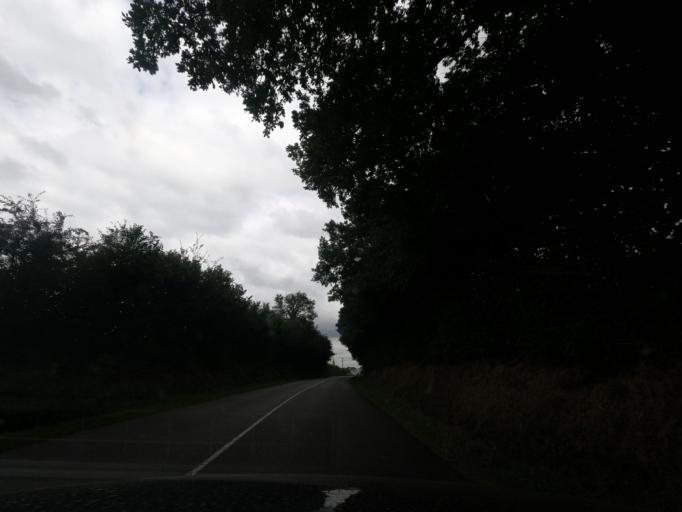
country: FR
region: Lower Normandy
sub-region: Departement de l'Orne
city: Briouze
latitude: 48.6923
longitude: -0.3768
